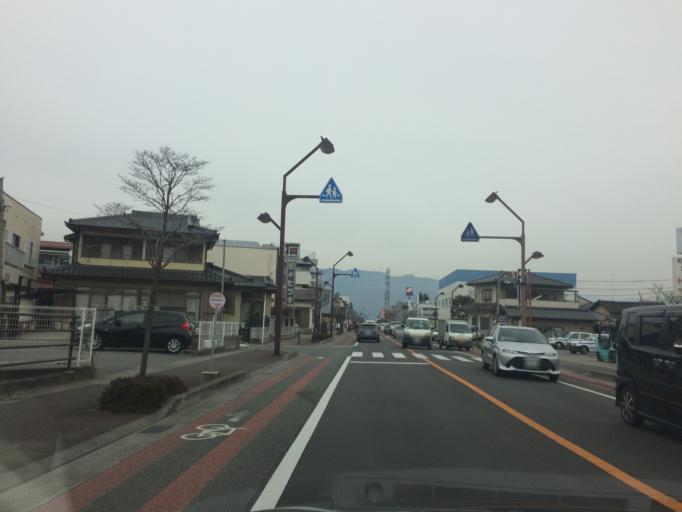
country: JP
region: Yamanashi
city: Kofu-shi
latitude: 35.6395
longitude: 138.5543
